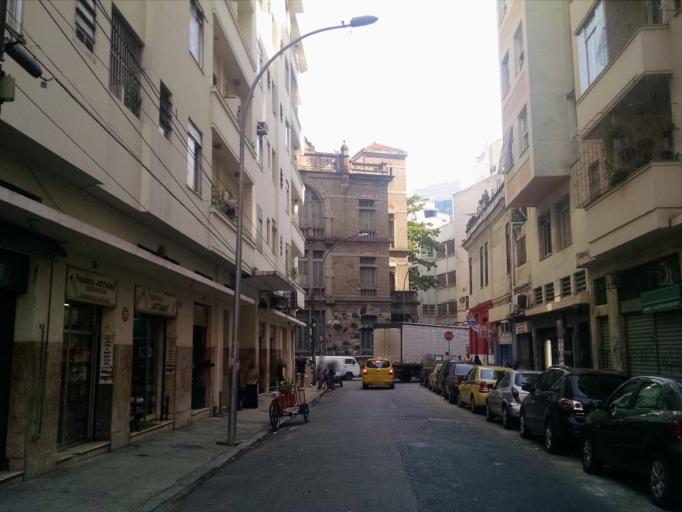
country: BR
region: Rio de Janeiro
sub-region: Rio De Janeiro
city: Rio de Janeiro
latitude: -22.9141
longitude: -43.1869
